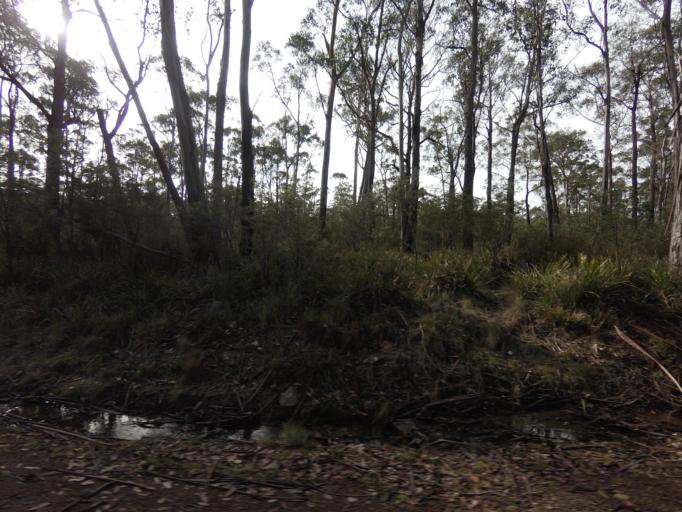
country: AU
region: Tasmania
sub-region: Derwent Valley
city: New Norfolk
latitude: -42.7670
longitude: 146.8995
